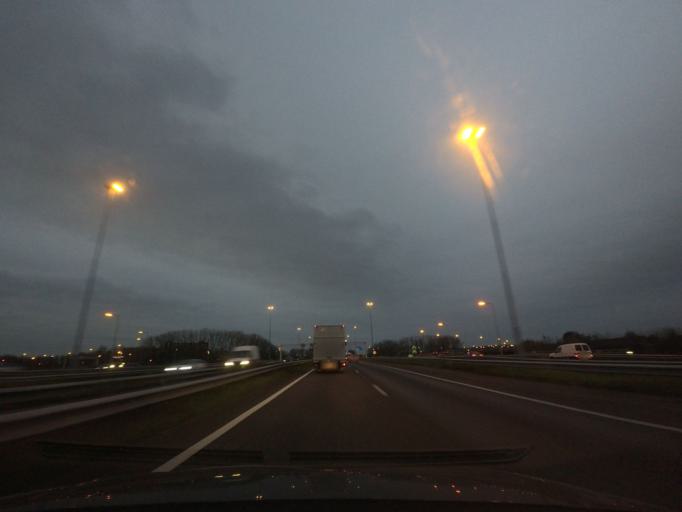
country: NL
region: South Holland
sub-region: Gemeente Gorinchem
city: Gorinchem
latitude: 51.8496
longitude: 4.9521
